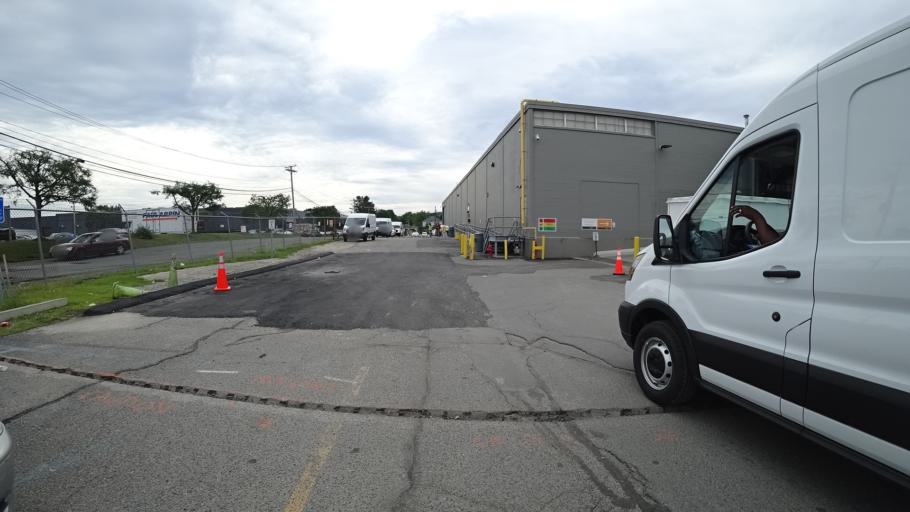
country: US
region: Massachusetts
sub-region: Norfolk County
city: Dedham
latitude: 42.2344
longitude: -71.1409
